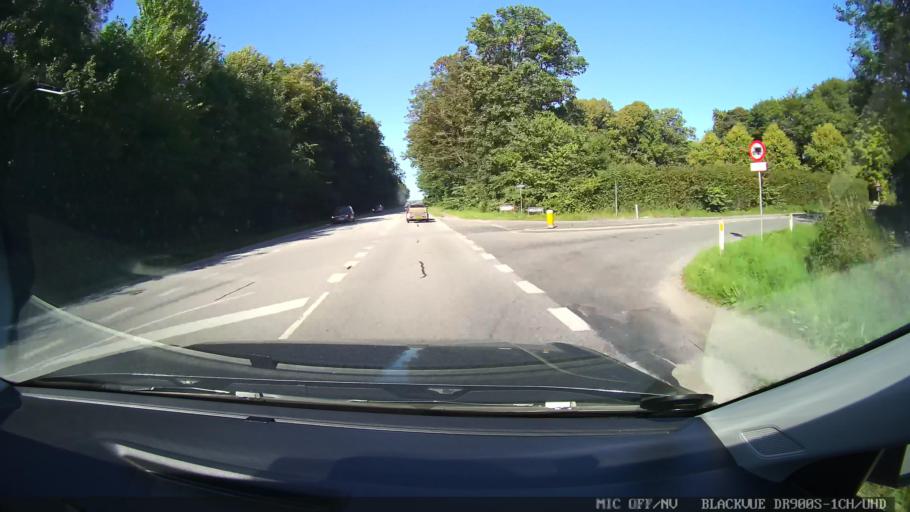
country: DK
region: Central Jutland
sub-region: Randers Kommune
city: Spentrup
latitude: 56.5049
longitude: 10.0220
